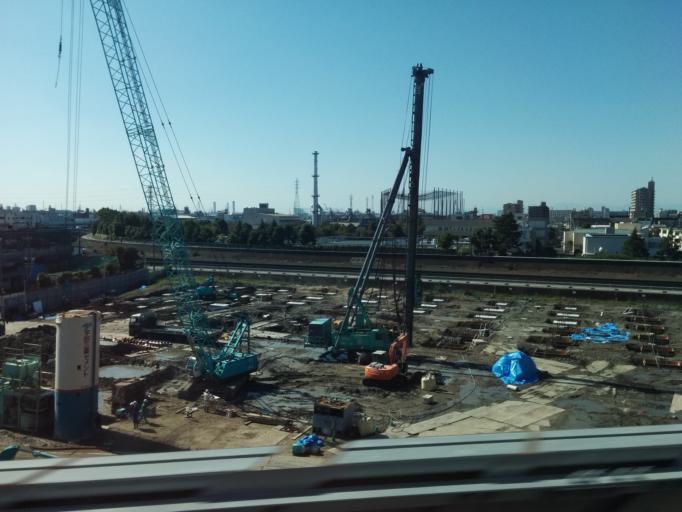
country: JP
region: Aichi
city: Nagoya-shi
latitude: 35.1013
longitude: 136.9227
